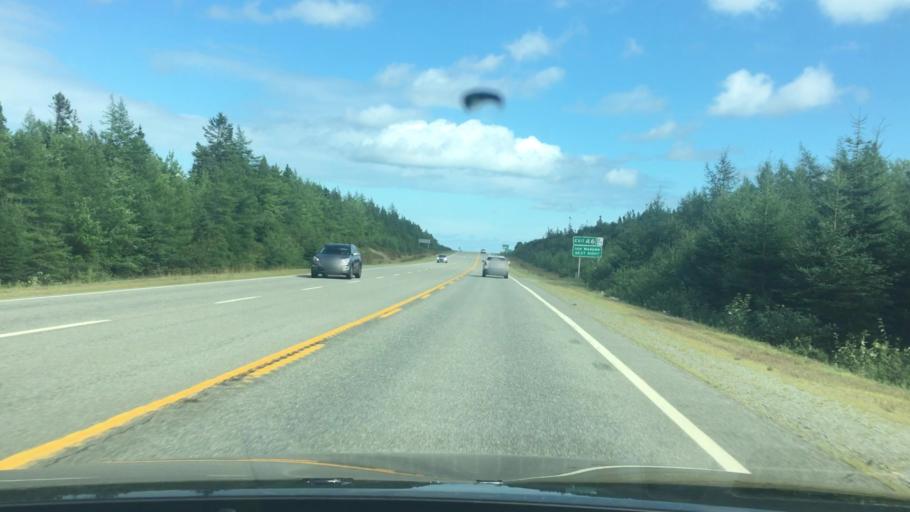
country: CA
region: Nova Scotia
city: Port Hawkesbury
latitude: 45.6154
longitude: -61.0972
